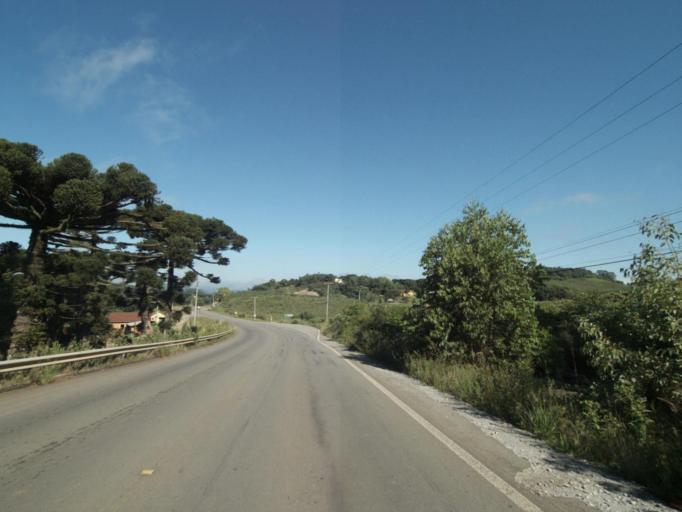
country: BR
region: Rio Grande do Sul
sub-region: Bento Goncalves
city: Bento Goncalves
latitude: -29.1157
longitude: -51.5763
